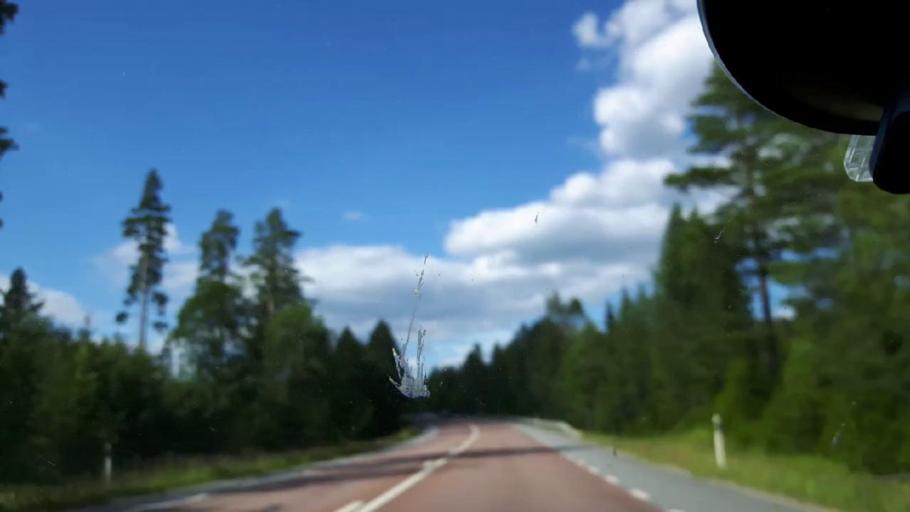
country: SE
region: Jaemtland
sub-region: Braecke Kommun
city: Braecke
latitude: 62.7651
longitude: 15.4077
